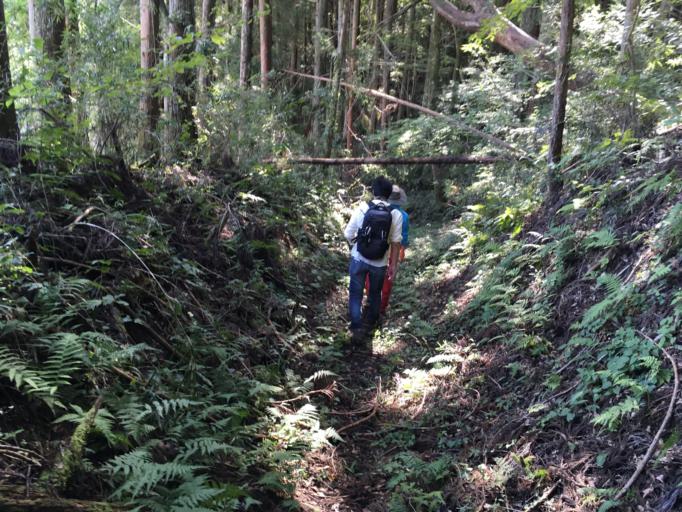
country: JP
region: Iwate
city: Ichinoseki
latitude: 38.8729
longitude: 141.1268
